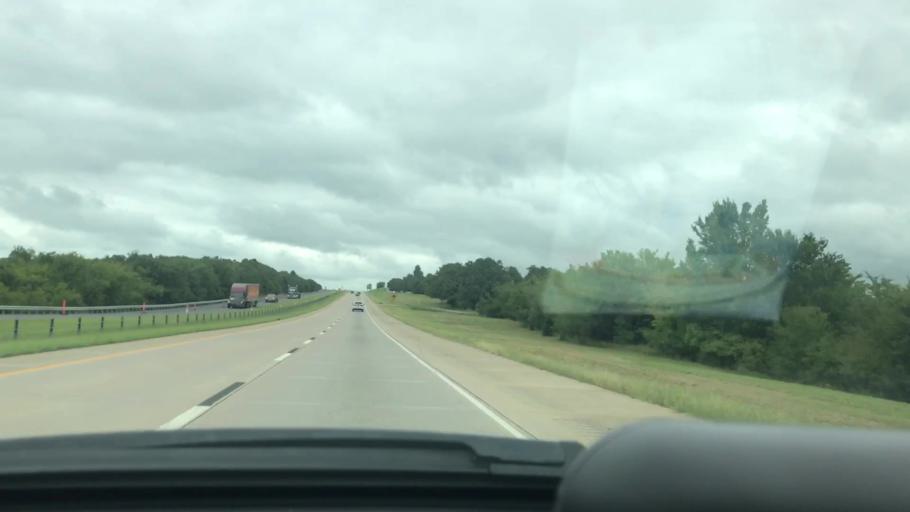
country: US
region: Oklahoma
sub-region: Pittsburg County
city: Krebs
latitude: 34.9805
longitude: -95.7227
